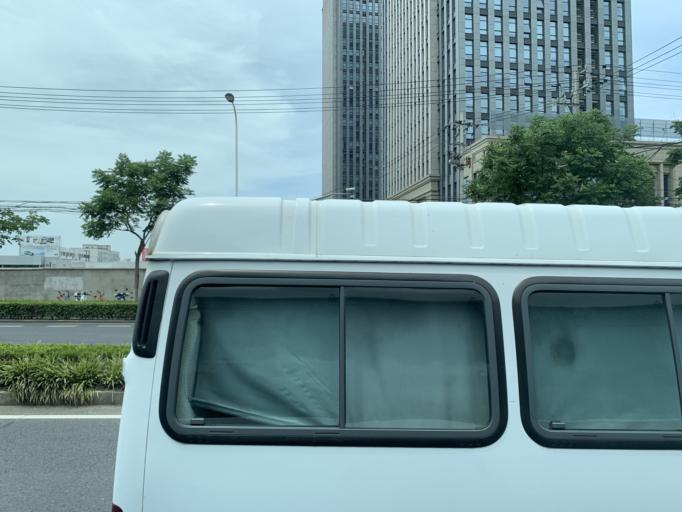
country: CN
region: Shanghai Shi
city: Kangqiao
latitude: 31.1603
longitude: 121.5598
